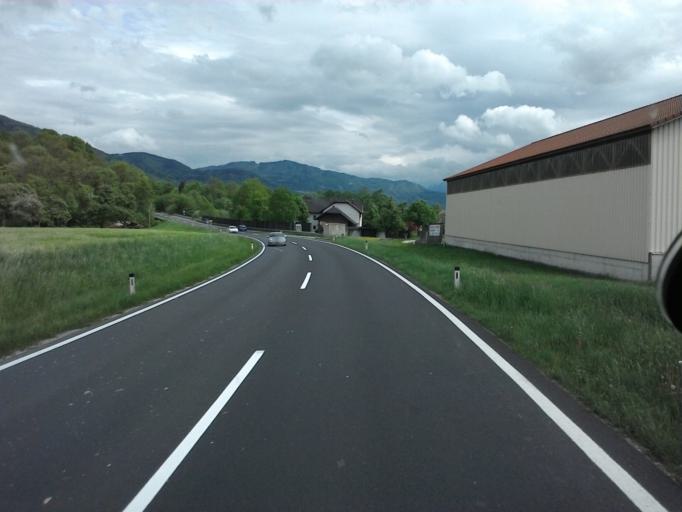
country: AT
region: Upper Austria
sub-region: Politischer Bezirk Kirchdorf an der Krems
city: Micheldorf in Oberoesterreich
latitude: 47.9247
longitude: 14.0907
